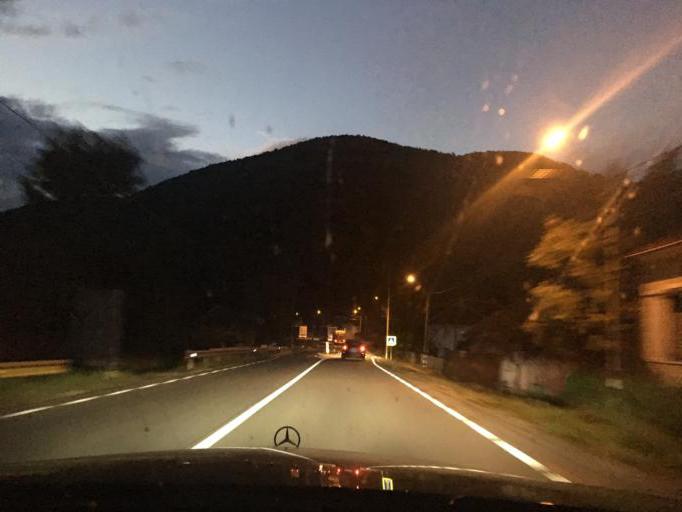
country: RO
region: Cluj
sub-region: Comuna Ciucea
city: Ciucea
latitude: 46.9565
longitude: 22.8105
